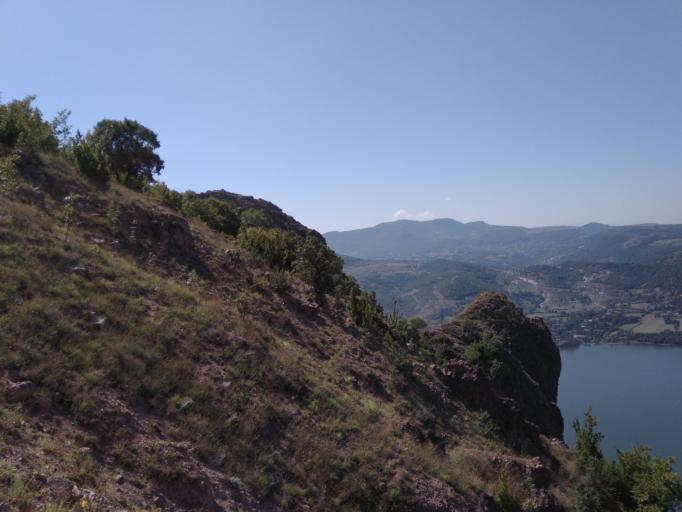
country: BG
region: Kurdzhali
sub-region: Obshtina Kurdzhali
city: Kurdzhali
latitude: 41.6248
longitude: 25.4569
